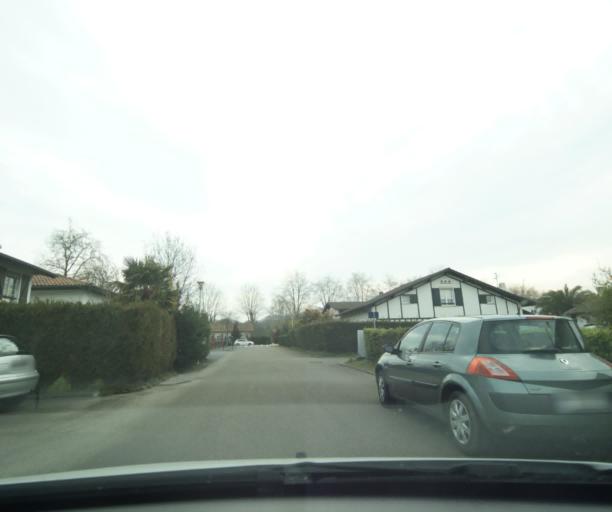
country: FR
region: Aquitaine
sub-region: Departement des Pyrenees-Atlantiques
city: Urrugne
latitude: 43.3637
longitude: -1.6945
